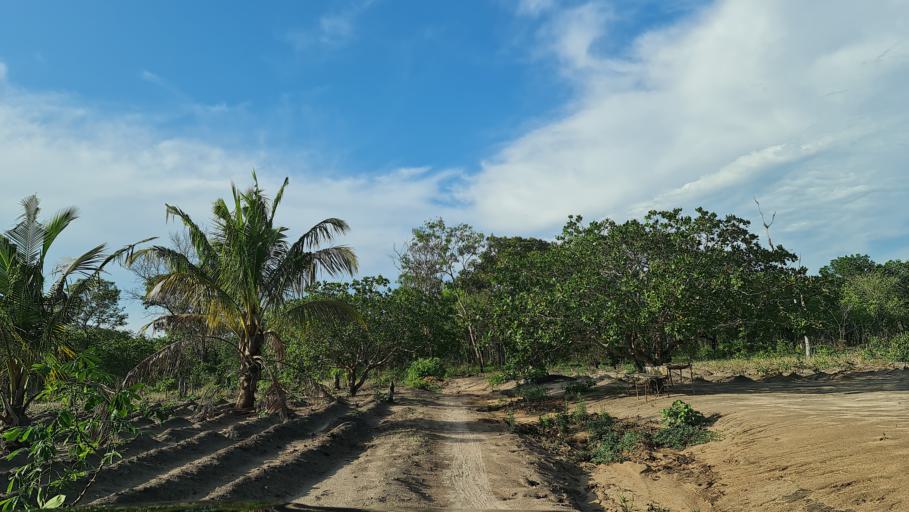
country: MZ
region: Zambezia
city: Quelimane
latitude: -17.1946
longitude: 37.4163
